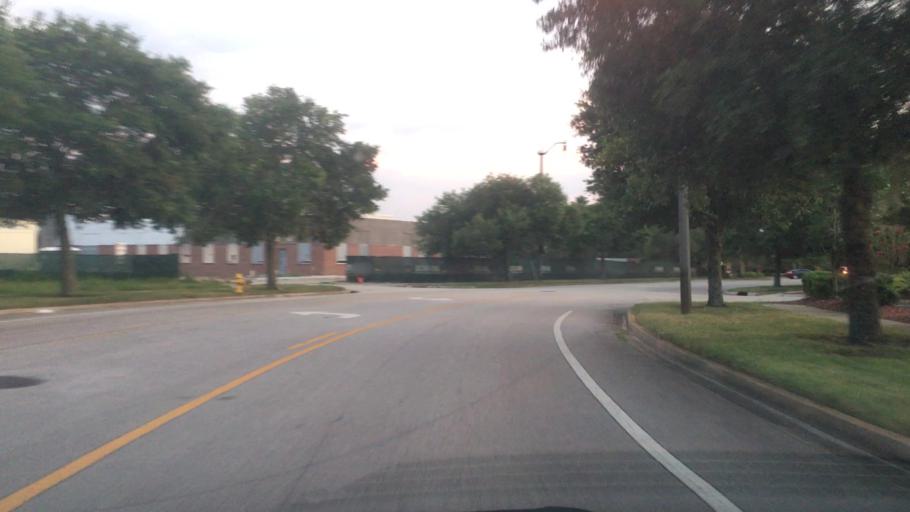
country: US
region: Florida
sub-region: Duval County
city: Jacksonville
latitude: 30.3403
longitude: -81.5449
